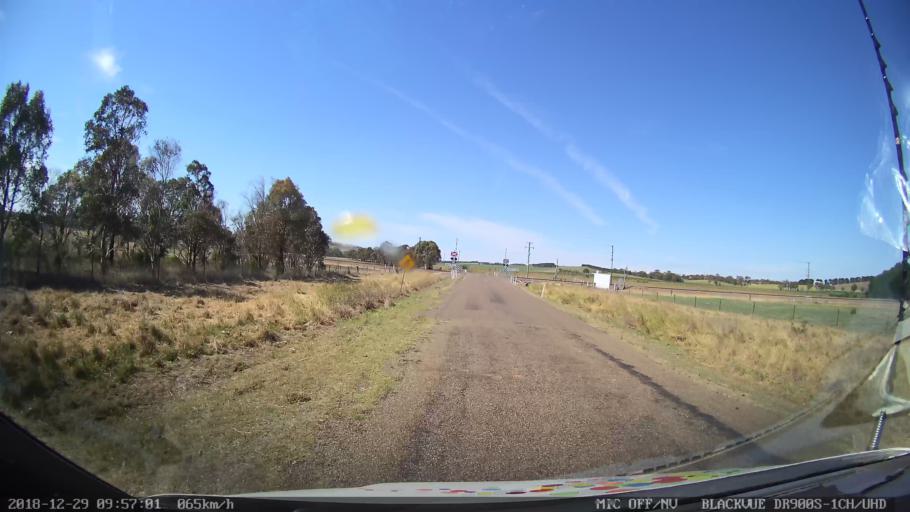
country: AU
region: New South Wales
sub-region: Goulburn Mulwaree
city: Goulburn
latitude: -34.7828
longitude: 149.4812
